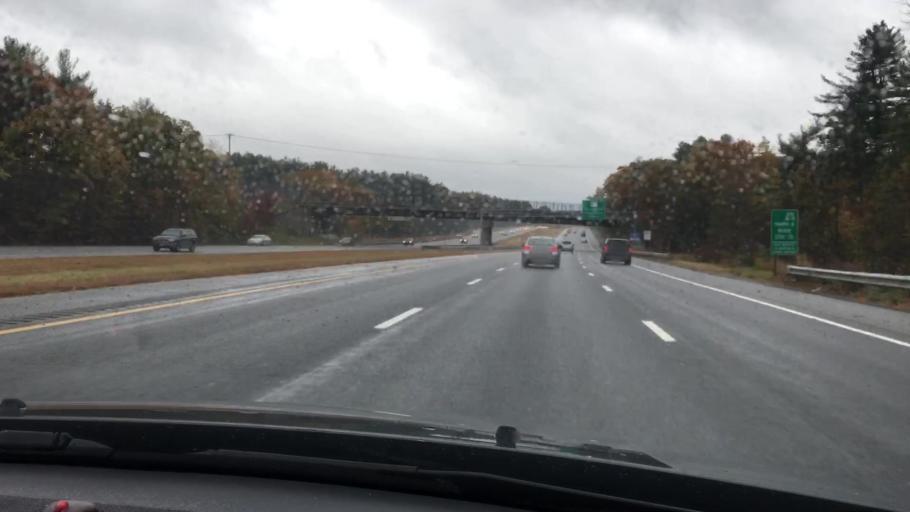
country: US
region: Massachusetts
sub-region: Middlesex County
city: Tyngsboro
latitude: 42.6875
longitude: -71.4431
